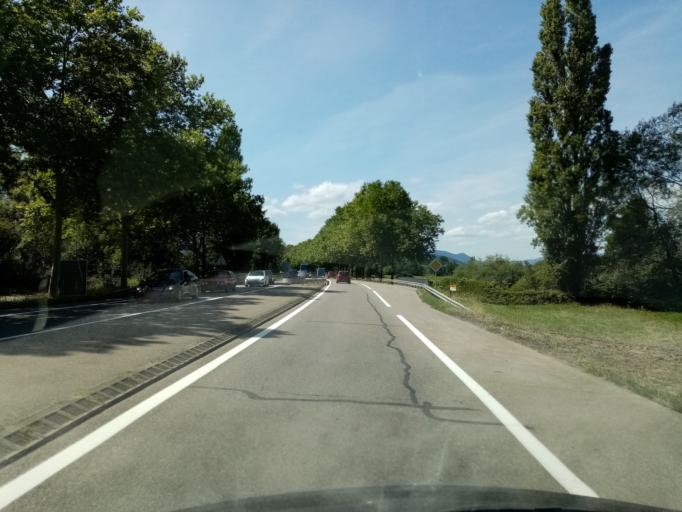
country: FR
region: Alsace
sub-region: Departement du Bas-Rhin
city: Selestat
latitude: 48.2467
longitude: 7.4585
